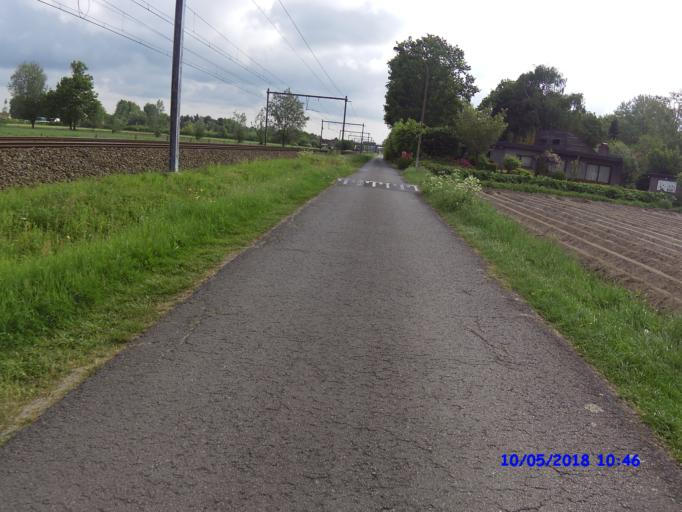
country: BE
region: Flanders
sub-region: Provincie Oost-Vlaanderen
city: De Pinte
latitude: 50.9922
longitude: 3.6249
